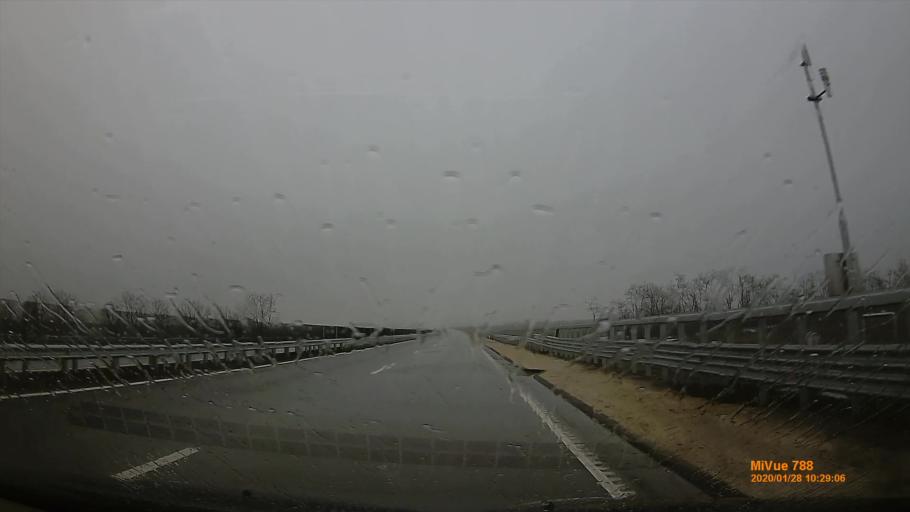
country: HU
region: Pest
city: Pilis
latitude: 47.3219
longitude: 19.5383
